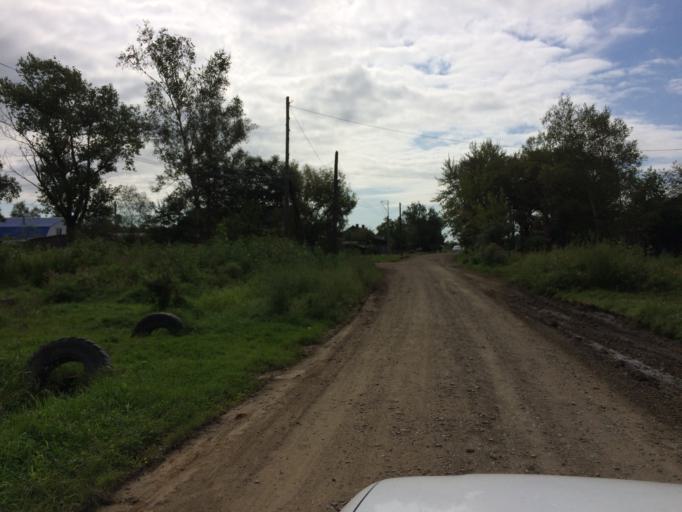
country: RU
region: Primorskiy
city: Dal'nerechensk
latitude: 45.9187
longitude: 133.7203
